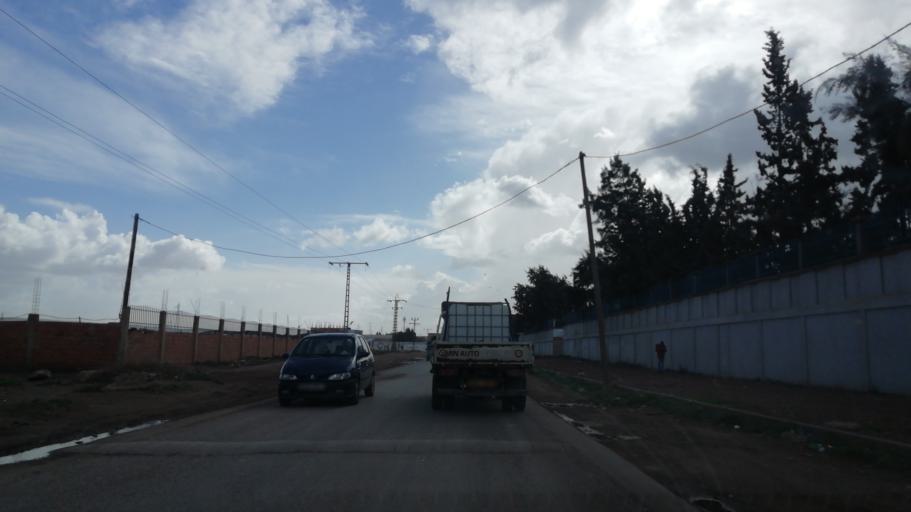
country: DZ
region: Oran
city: Sidi ech Chahmi
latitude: 35.6419
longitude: -0.5540
